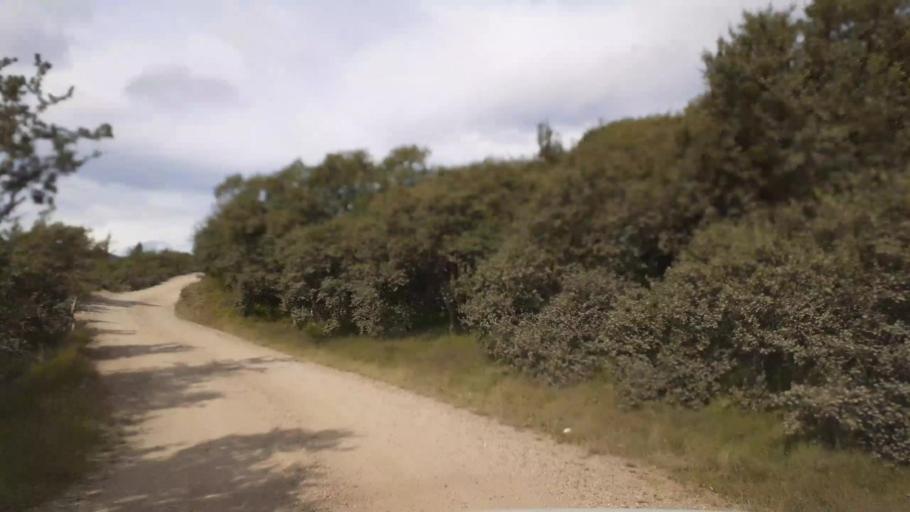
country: IS
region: East
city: Hoefn
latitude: 64.4397
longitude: -14.9179
